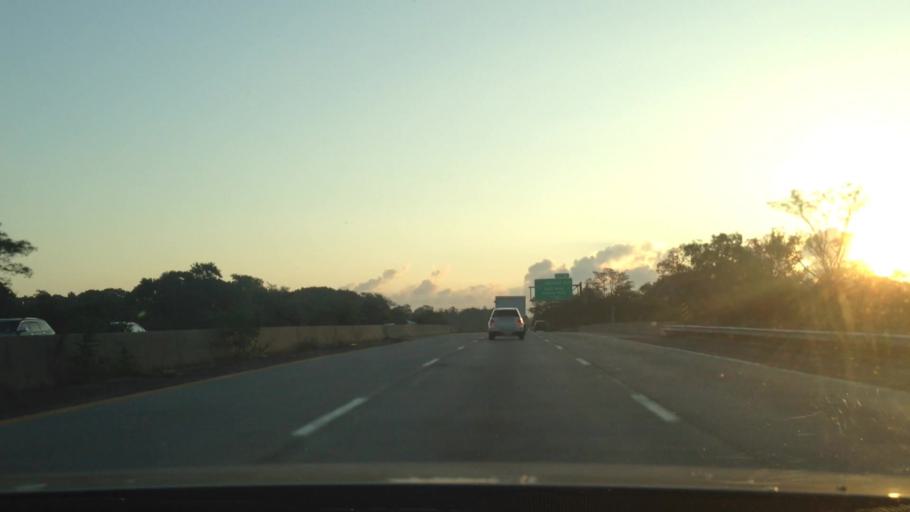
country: US
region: New York
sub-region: Suffolk County
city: Islip
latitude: 40.7412
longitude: -73.2153
